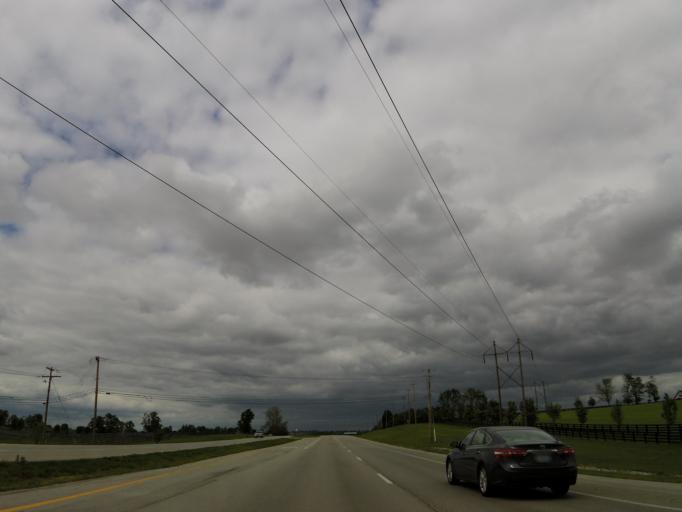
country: US
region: Kentucky
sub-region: Scott County
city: Georgetown
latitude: 38.1760
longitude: -84.5978
